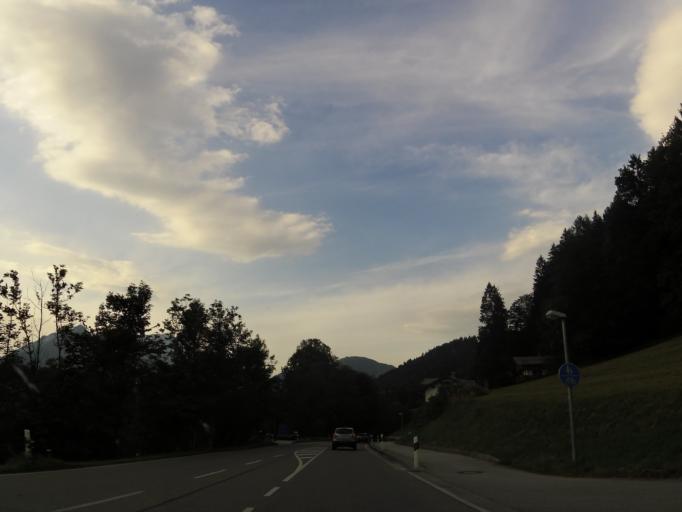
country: DE
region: Bavaria
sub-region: Upper Bavaria
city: Schoenau am Koenigssee
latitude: 47.6127
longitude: 12.9993
